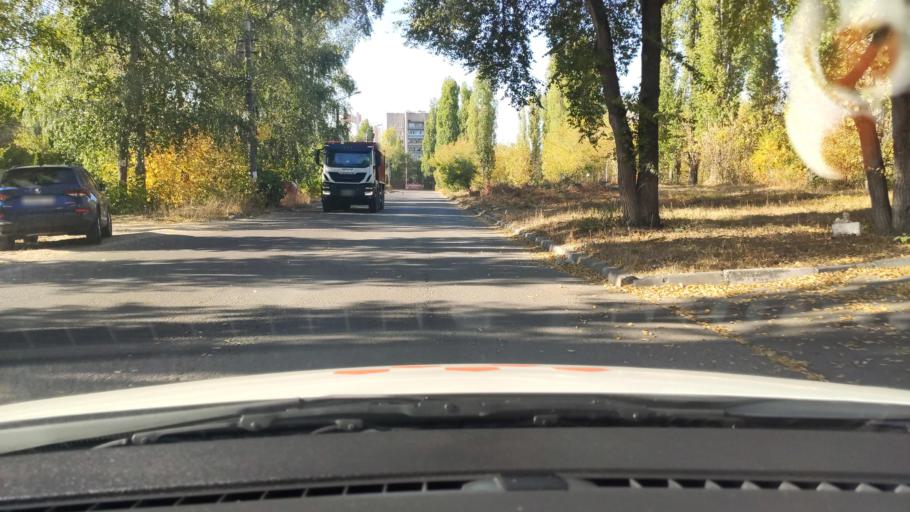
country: RU
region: Voronezj
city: Voronezh
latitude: 51.6827
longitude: 39.1453
